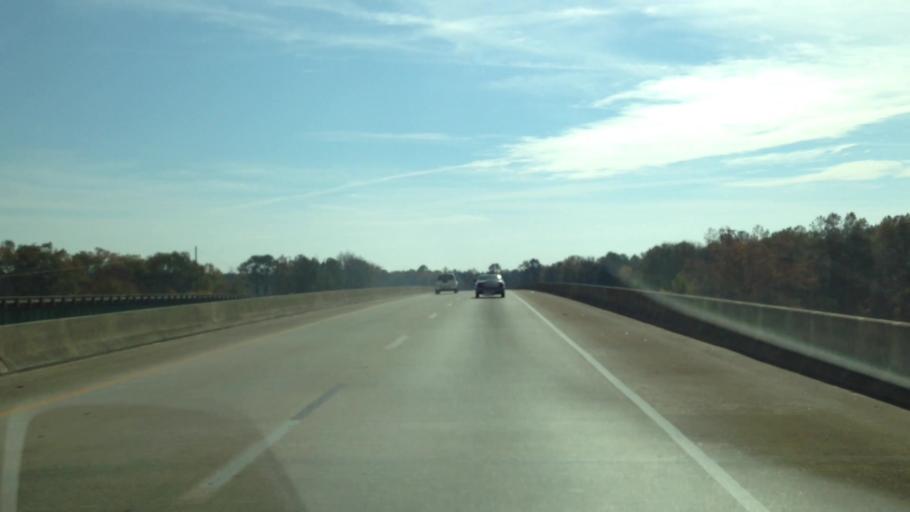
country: US
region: Alabama
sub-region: Autauga County
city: Prattville
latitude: 32.4119
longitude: -86.4086
